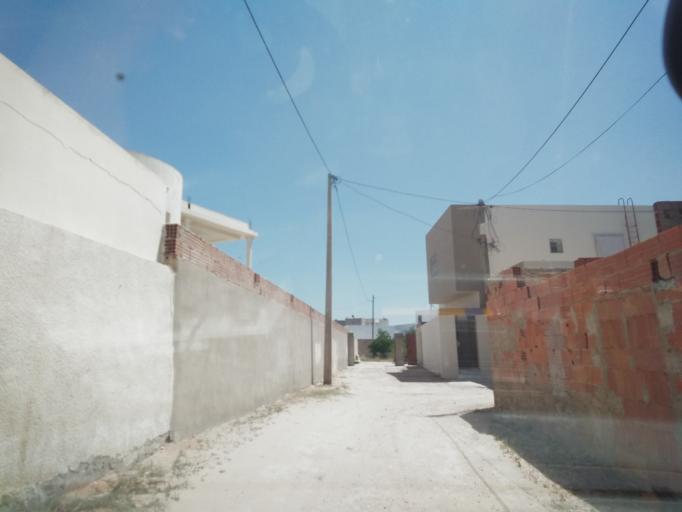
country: TN
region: Safaqis
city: Al Qarmadah
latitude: 34.8204
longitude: 10.7633
